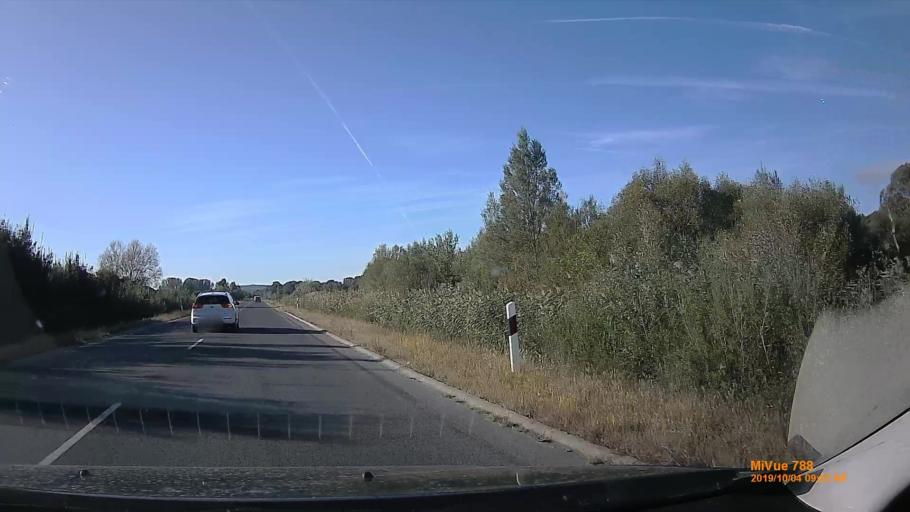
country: HU
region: Somogy
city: Karad
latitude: 46.7192
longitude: 17.7747
